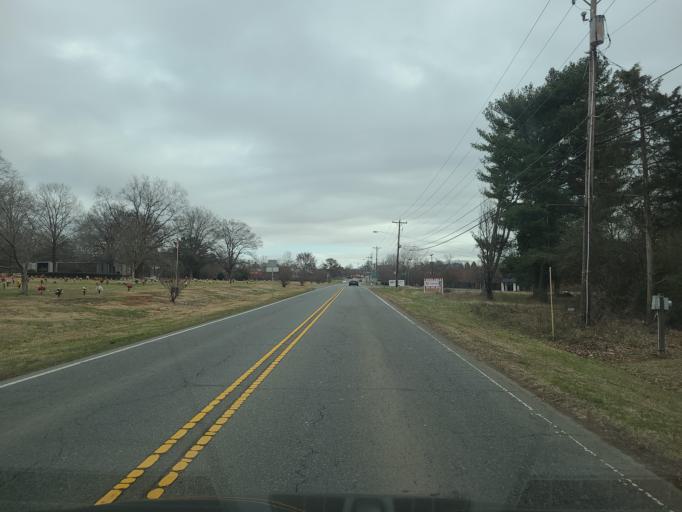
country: US
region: North Carolina
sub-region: Mecklenburg County
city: Mint Hill
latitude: 35.1888
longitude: -80.6943
